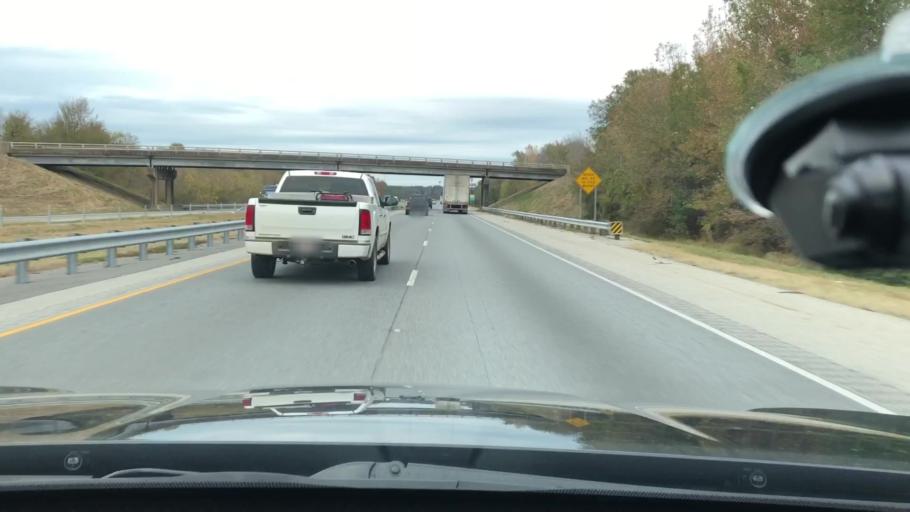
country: US
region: Arkansas
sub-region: Clark County
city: Arkadelphia
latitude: 34.1712
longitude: -93.0748
